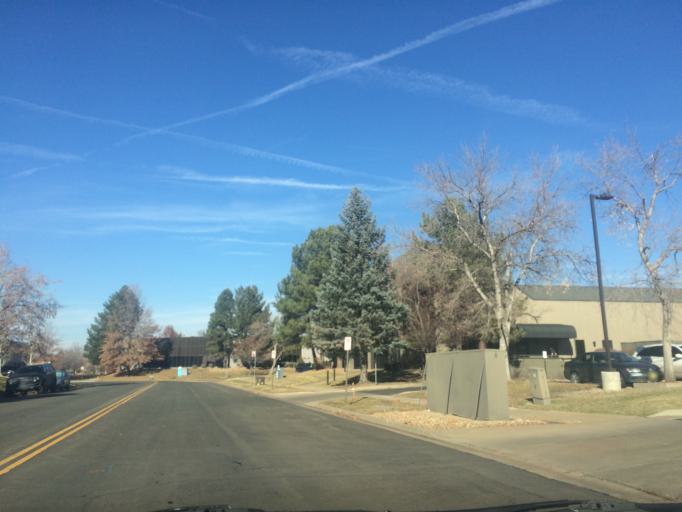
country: US
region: Colorado
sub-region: Boulder County
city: Boulder
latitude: 40.0246
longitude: -105.2184
